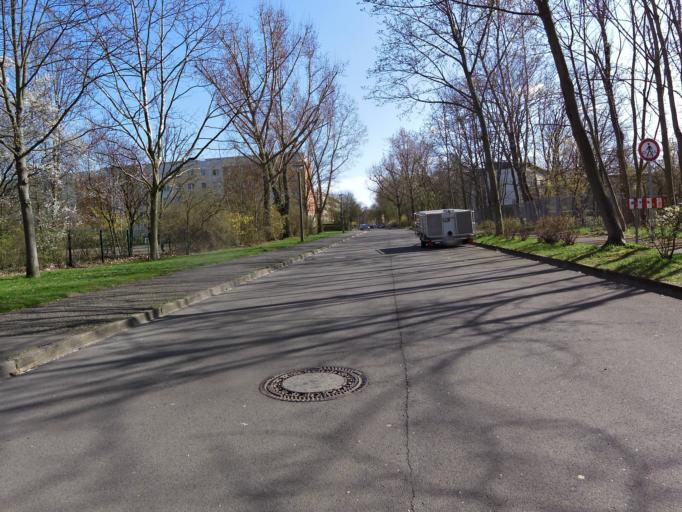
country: DE
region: Saxony
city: Leipzig
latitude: 51.3192
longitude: 12.3030
